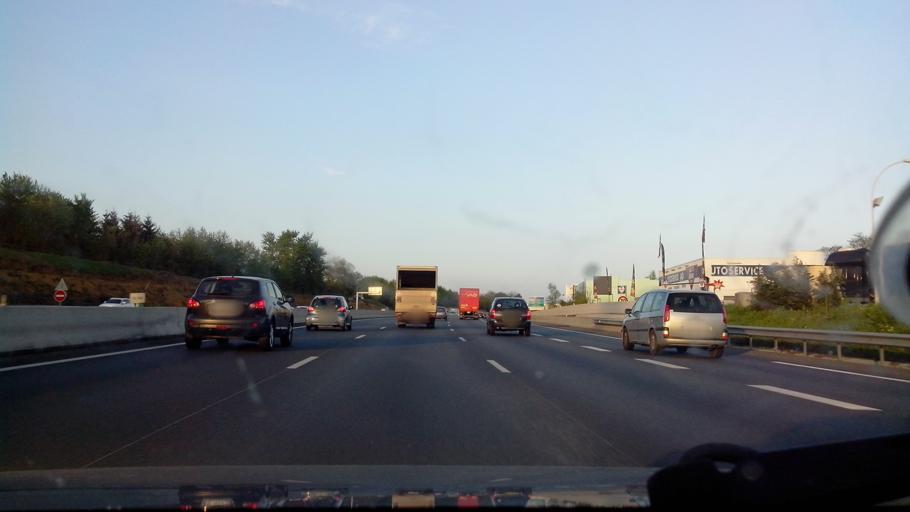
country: FR
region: Ile-de-France
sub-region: Departement de l'Essonne
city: Etiolles
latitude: 48.6305
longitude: 2.4863
